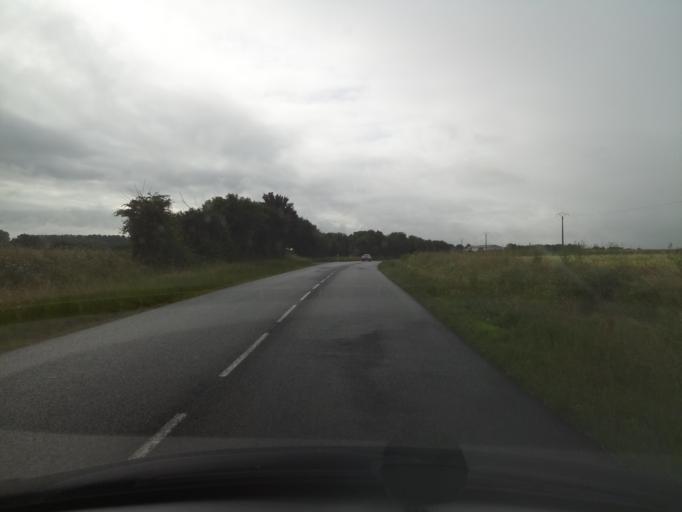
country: FR
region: Poitou-Charentes
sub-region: Departement de la Charente-Maritime
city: Surgeres
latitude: 46.1521
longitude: -0.8135
